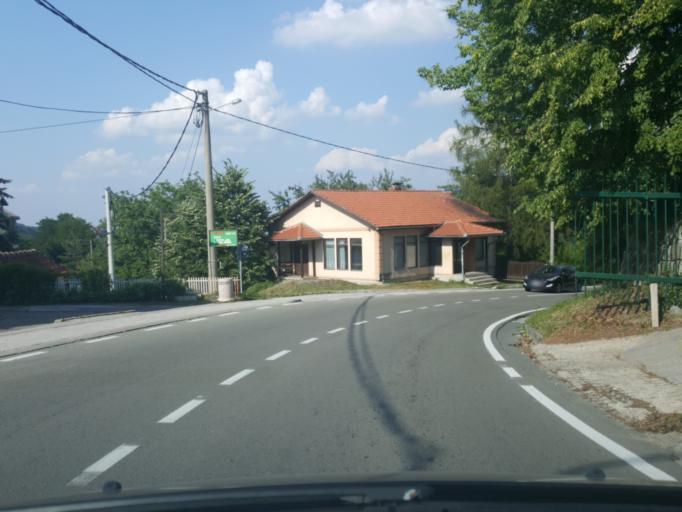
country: RS
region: Central Serbia
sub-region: Moravicki Okrug
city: Gornji Milanovac
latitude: 44.1395
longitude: 20.4941
